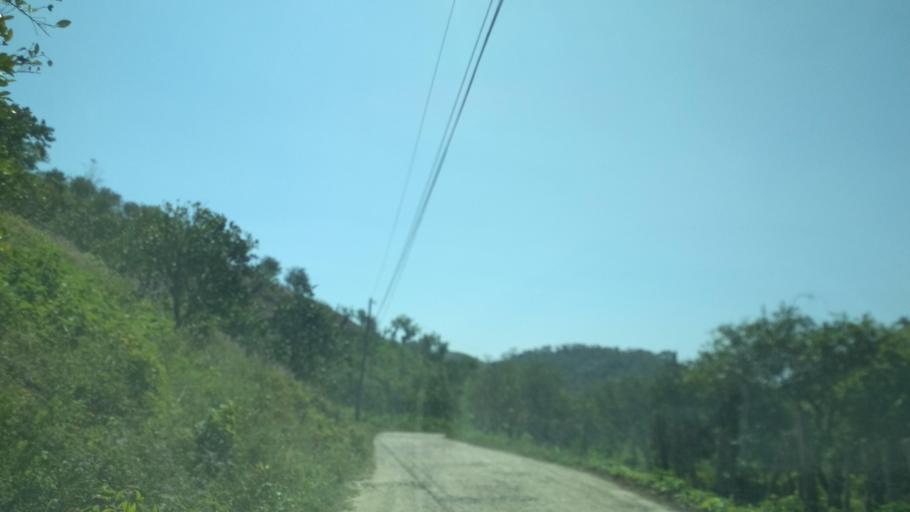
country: MX
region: Veracruz
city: Gutierrez Zamora
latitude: 20.4793
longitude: -97.1590
